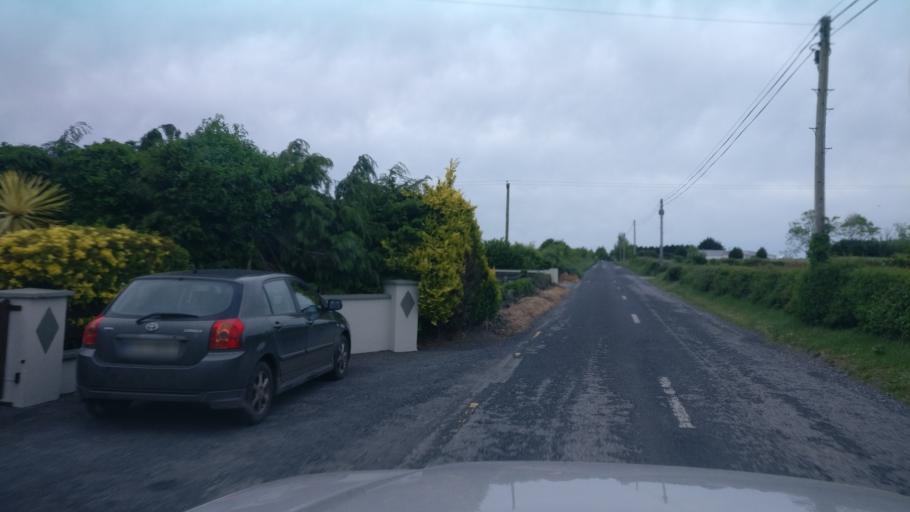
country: IE
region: Connaught
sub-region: County Galway
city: Portumna
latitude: 53.1107
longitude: -8.2731
